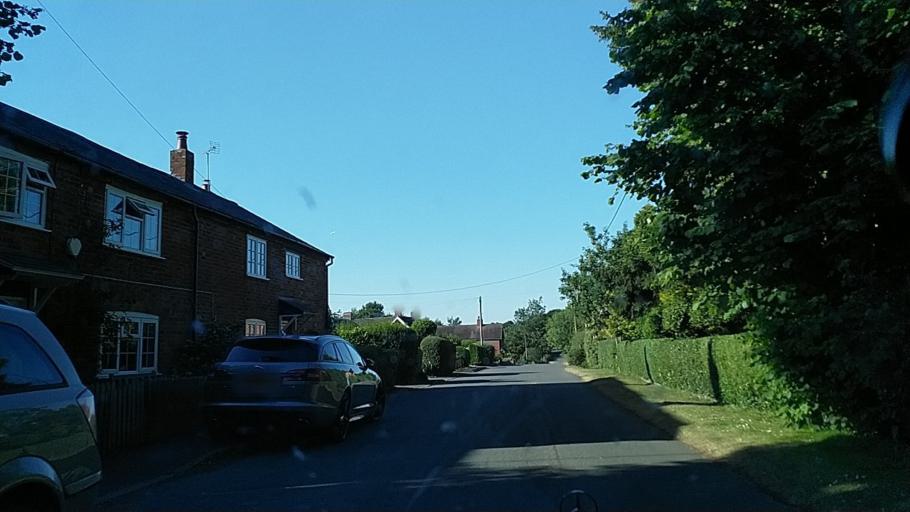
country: GB
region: England
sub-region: Warwickshire
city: Wroxall
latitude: 52.3381
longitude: -1.6578
